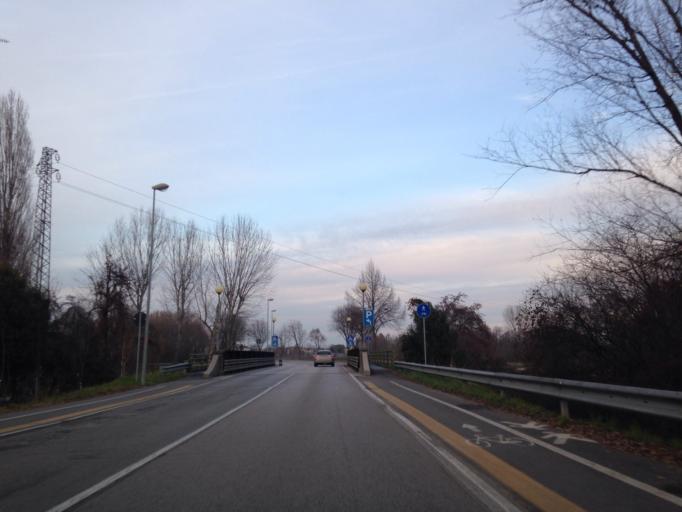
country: IT
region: Friuli Venezia Giulia
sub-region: Provincia di Pordenone
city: Sacile
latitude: 45.9518
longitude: 12.5097
